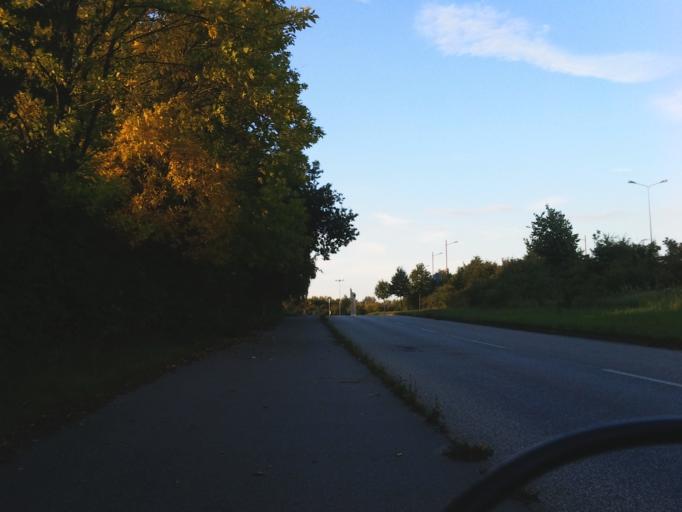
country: DE
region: Mecklenburg-Vorpommern
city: Lambrechtshagen
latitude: 54.1034
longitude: 12.0640
